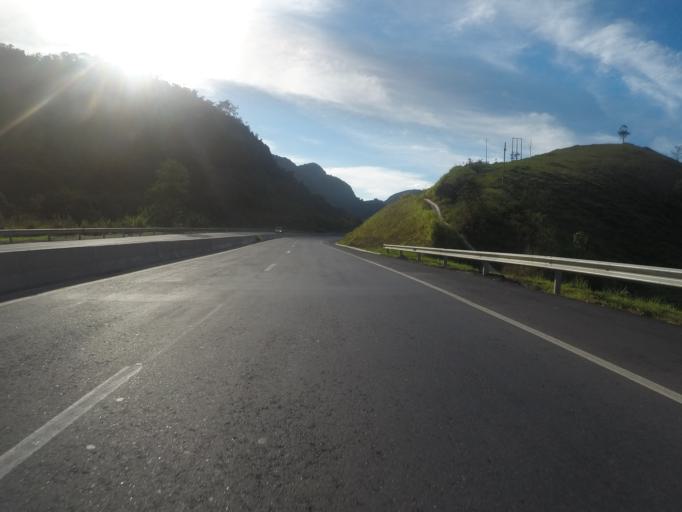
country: BR
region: Espirito Santo
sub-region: Ibiracu
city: Ibiracu
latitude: -19.8530
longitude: -40.3824
